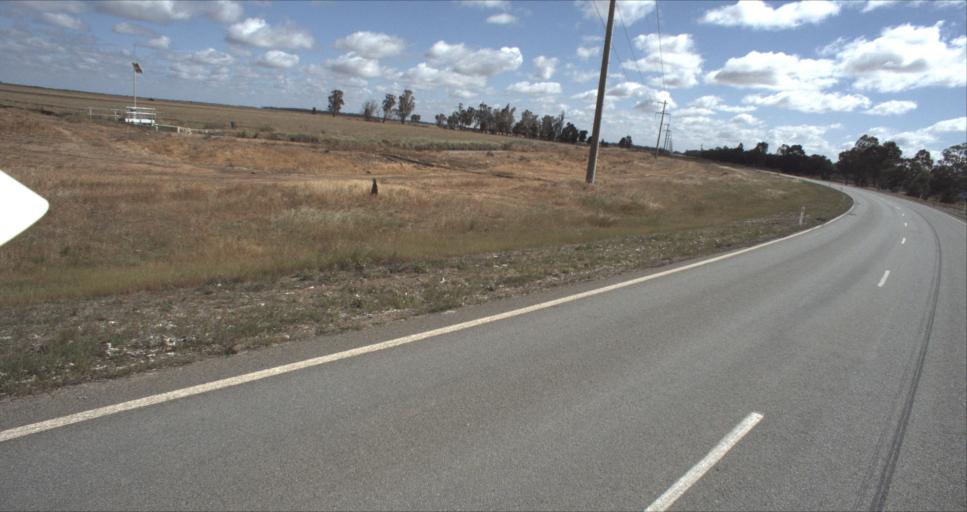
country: AU
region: New South Wales
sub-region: Murrumbidgee Shire
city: Darlington Point
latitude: -34.5963
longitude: 146.1622
